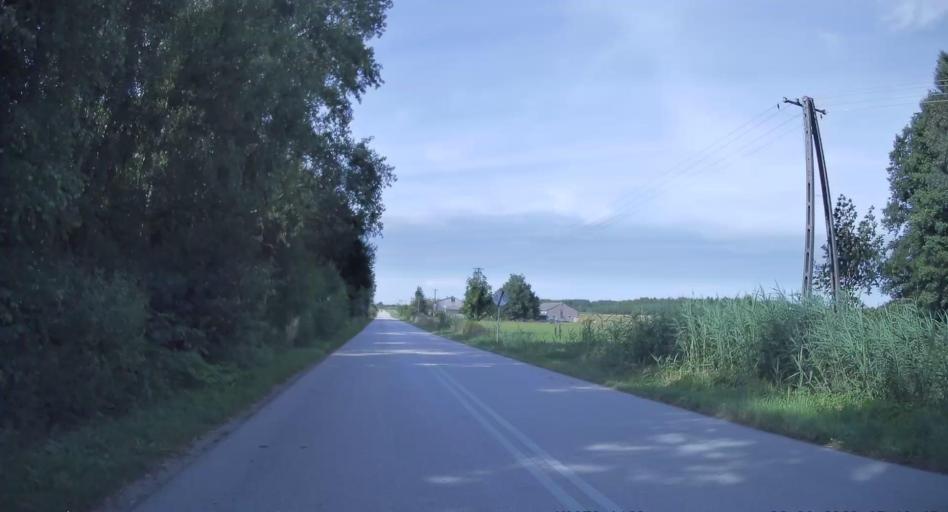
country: PL
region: Lodz Voivodeship
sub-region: Powiat opoczynski
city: Mniszkow
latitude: 51.3552
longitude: 20.0371
